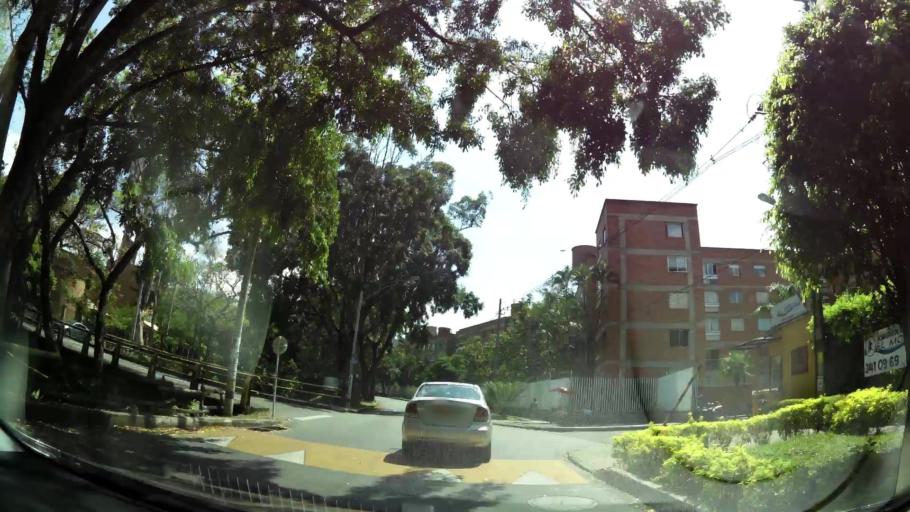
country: CO
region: Antioquia
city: Itagui
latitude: 6.2149
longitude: -75.5987
